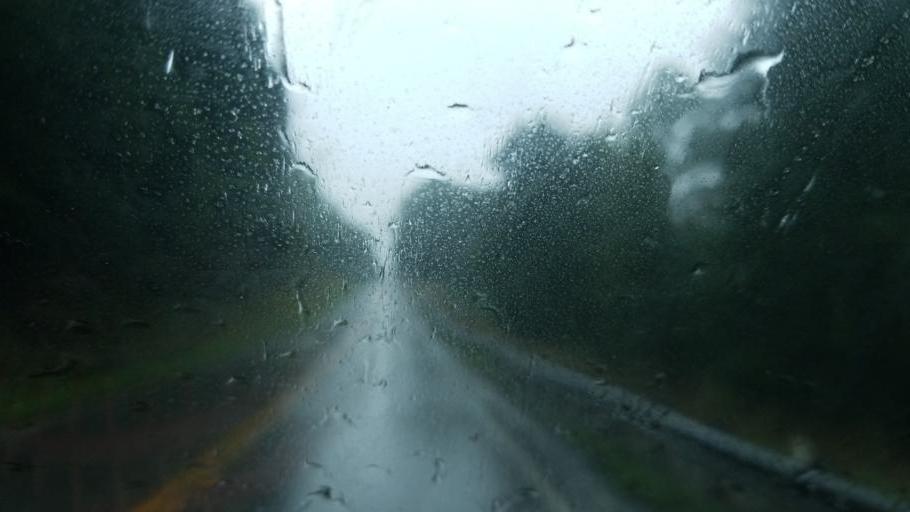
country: US
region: Kentucky
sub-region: Rowan County
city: Morehead
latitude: 38.2272
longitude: -83.4930
